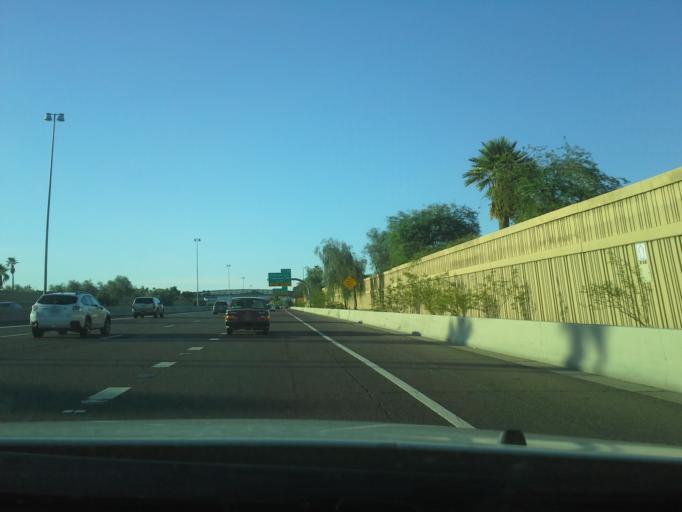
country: US
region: Arizona
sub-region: Maricopa County
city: Phoenix
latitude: 33.4989
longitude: -112.0435
